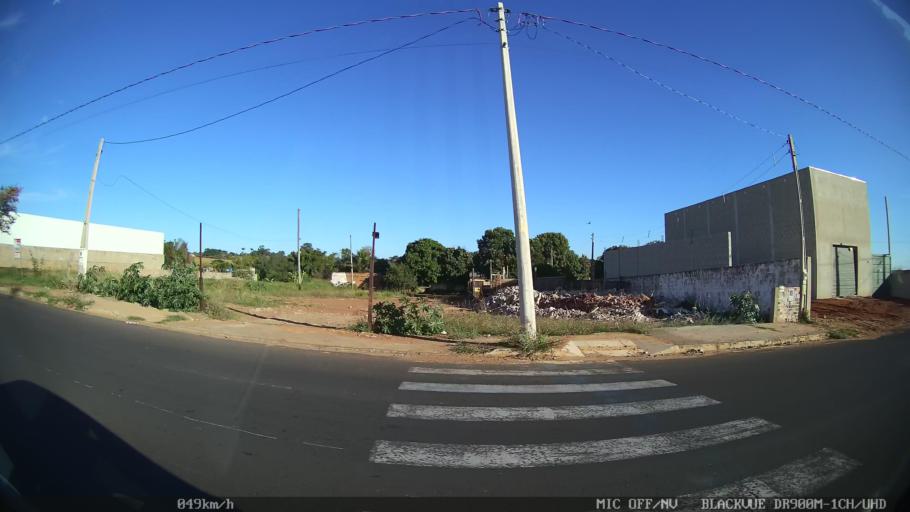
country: BR
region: Sao Paulo
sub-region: Americo Brasiliense
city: Americo Brasiliense
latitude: -21.7476
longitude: -48.1383
